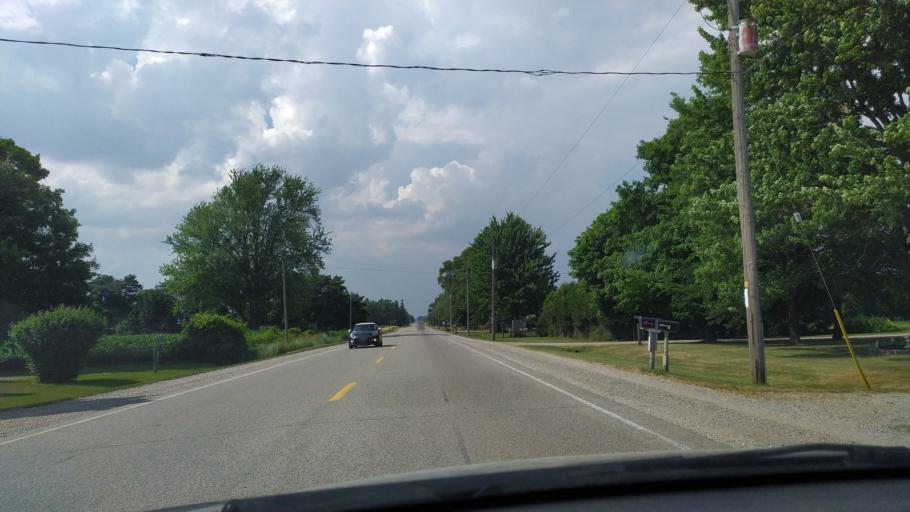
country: CA
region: Ontario
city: Dorchester
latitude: 43.0375
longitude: -81.1242
